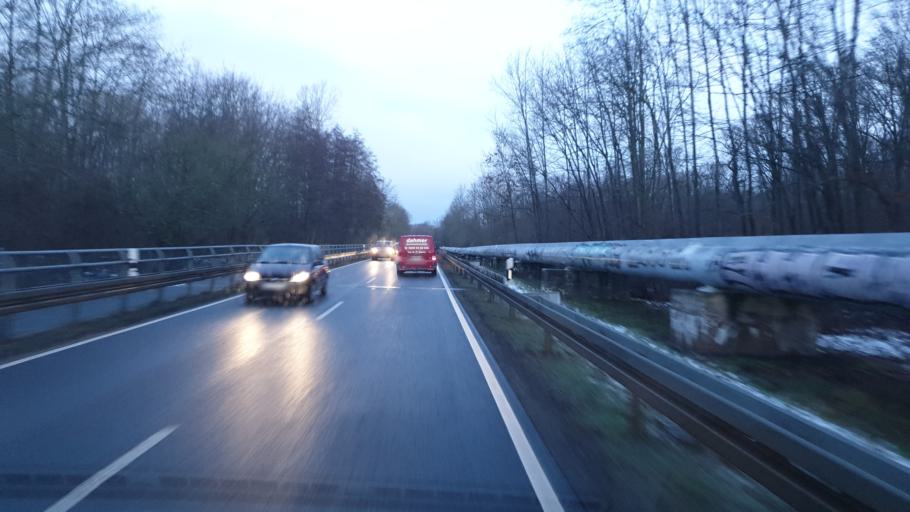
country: DE
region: Saxony
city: Markkleeberg
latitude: 51.2964
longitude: 12.3481
